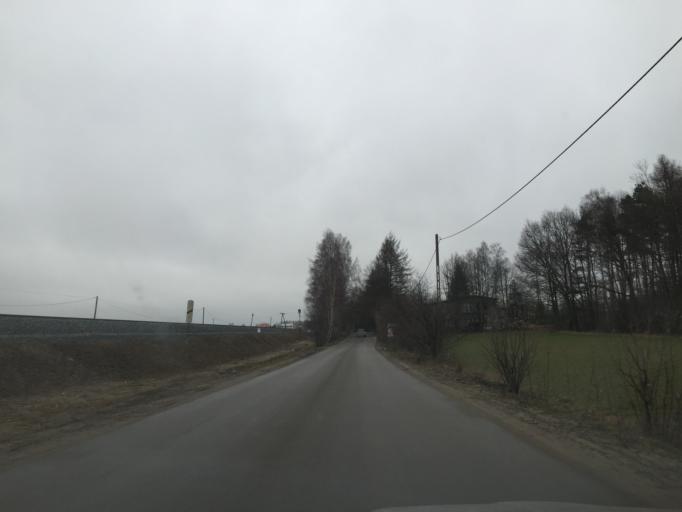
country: PL
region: Pomeranian Voivodeship
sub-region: Powiat kartuski
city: Banino
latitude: 54.4070
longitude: 18.4416
